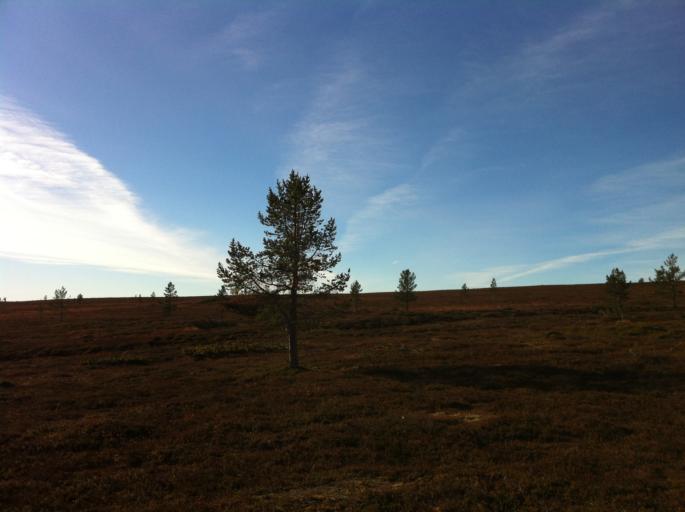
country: NO
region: Hedmark
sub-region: Engerdal
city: Engerdal
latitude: 62.1123
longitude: 12.2731
